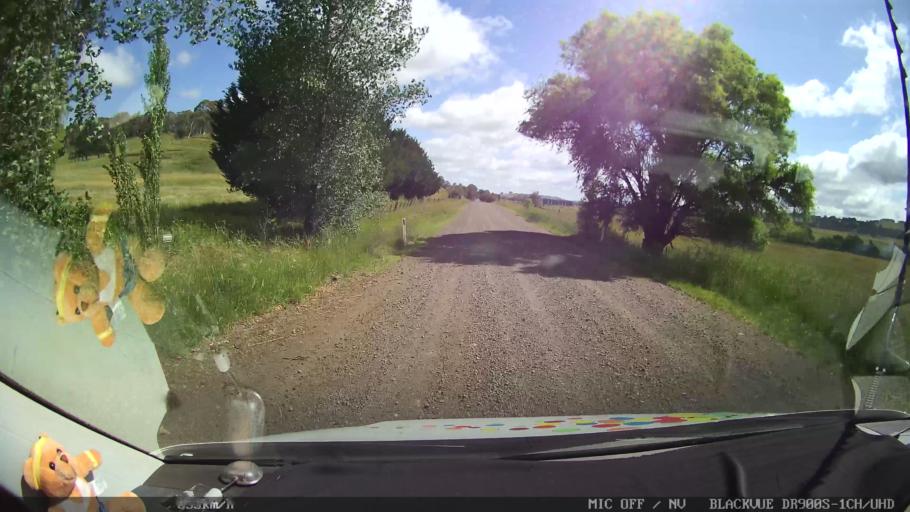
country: AU
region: New South Wales
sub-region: Glen Innes Severn
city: Glen Innes
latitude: -29.9594
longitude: 151.7015
